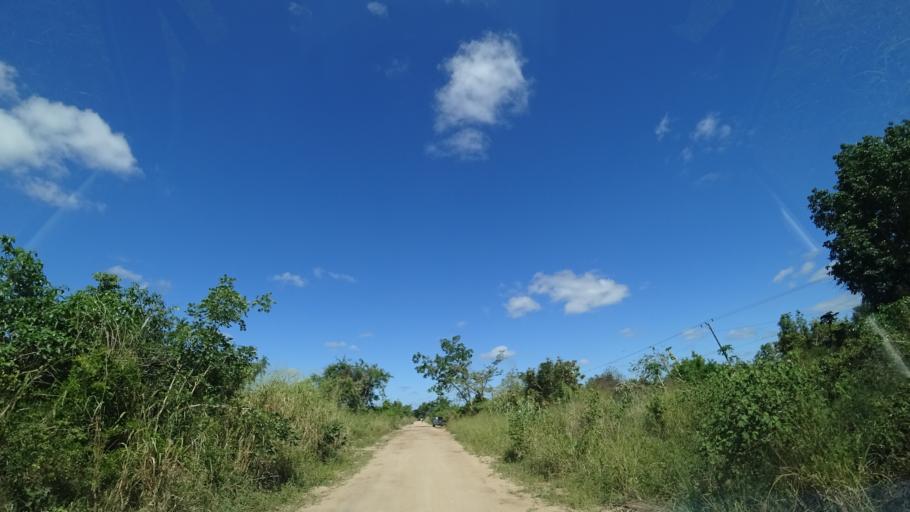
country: MZ
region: Sofala
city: Dondo
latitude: -19.3230
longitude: 34.6919
